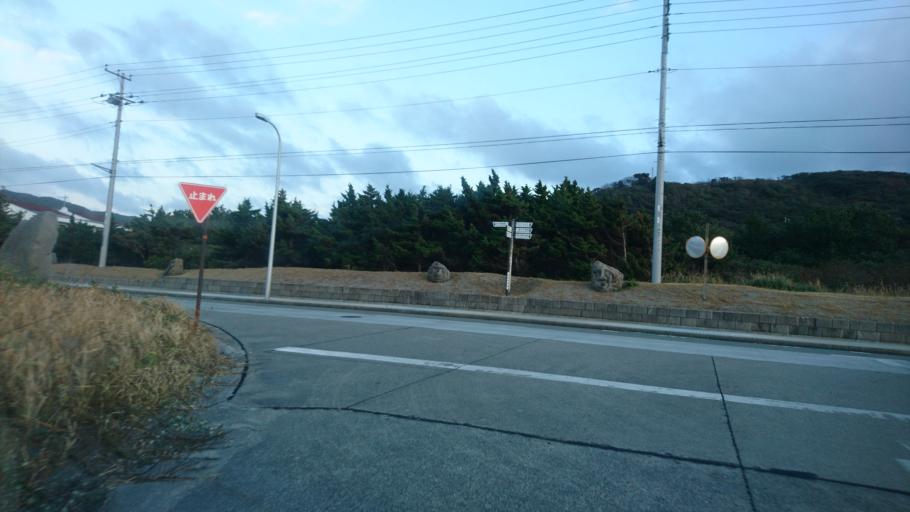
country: JP
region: Shizuoka
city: Shimoda
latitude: 34.3720
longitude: 139.2505
